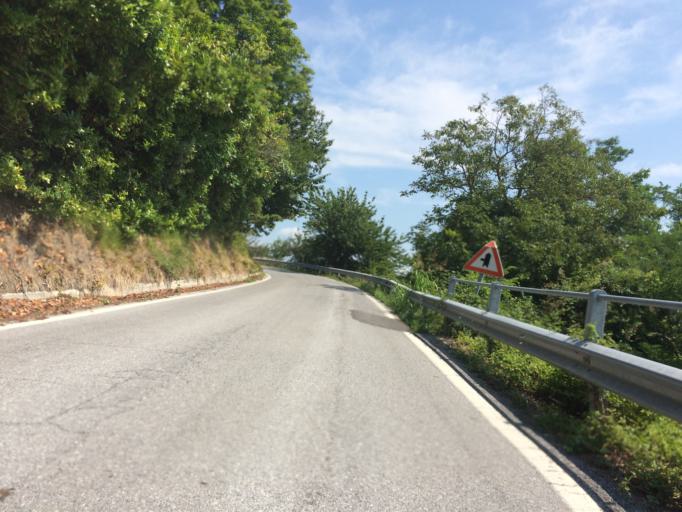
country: IT
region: Piedmont
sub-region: Provincia di Cuneo
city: Serravalle Langhe
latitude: 44.5586
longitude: 8.0494
